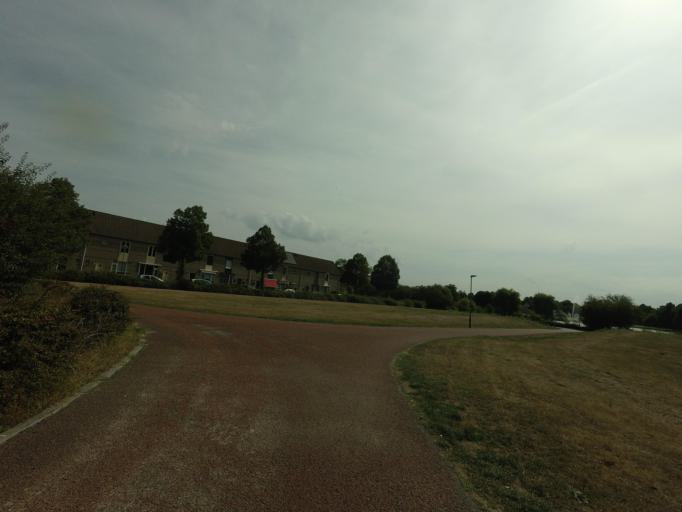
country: NL
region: North Brabant
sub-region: Gemeente Helmond
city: Helmond
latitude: 51.4647
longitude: 5.7021
